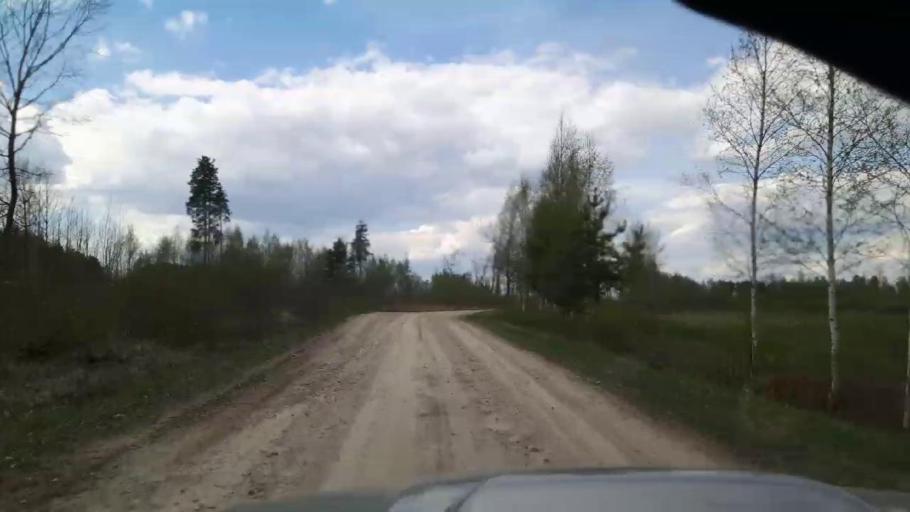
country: EE
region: Paernumaa
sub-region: Sindi linn
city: Sindi
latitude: 58.4086
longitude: 24.6931
